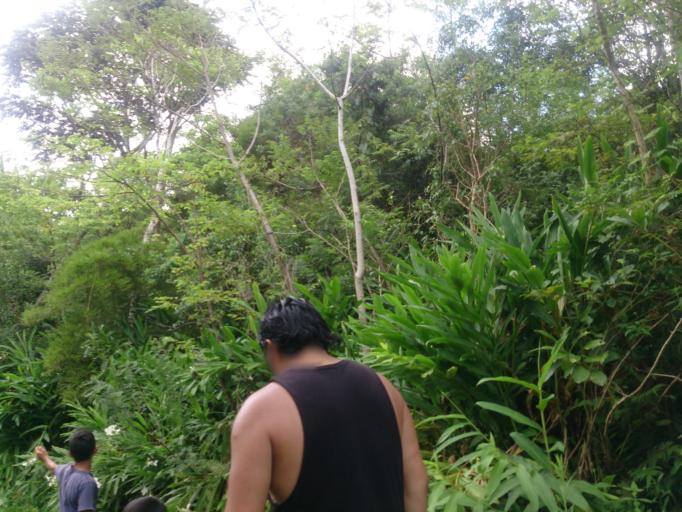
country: AR
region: Misiones
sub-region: Departamento de Obera
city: Obera
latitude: -27.5102
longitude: -55.1072
